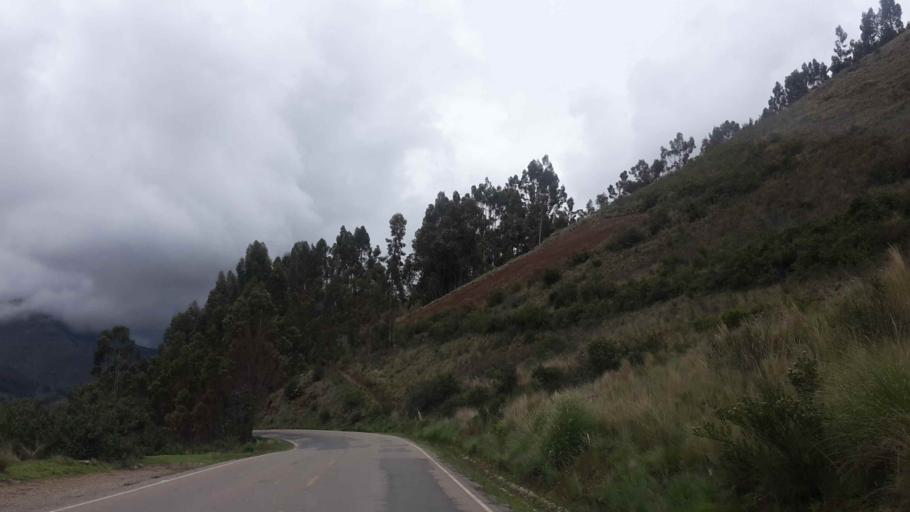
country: BO
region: Cochabamba
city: Arani
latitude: -17.4774
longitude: -65.5319
